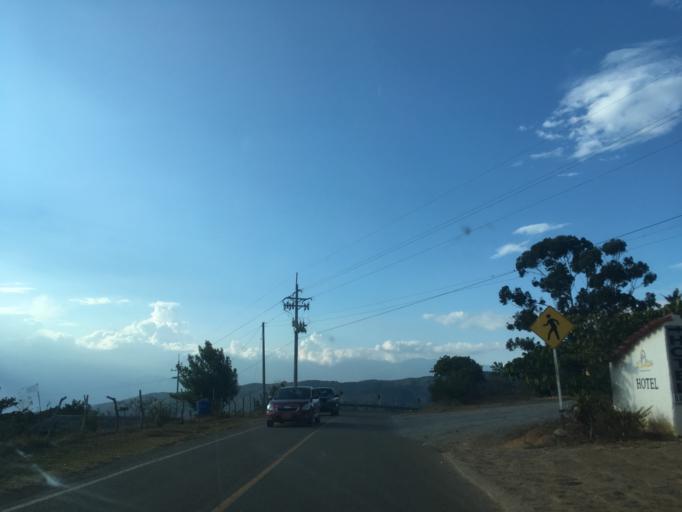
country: CO
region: Santander
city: Villanueva
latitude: 6.6312
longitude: -73.1789
